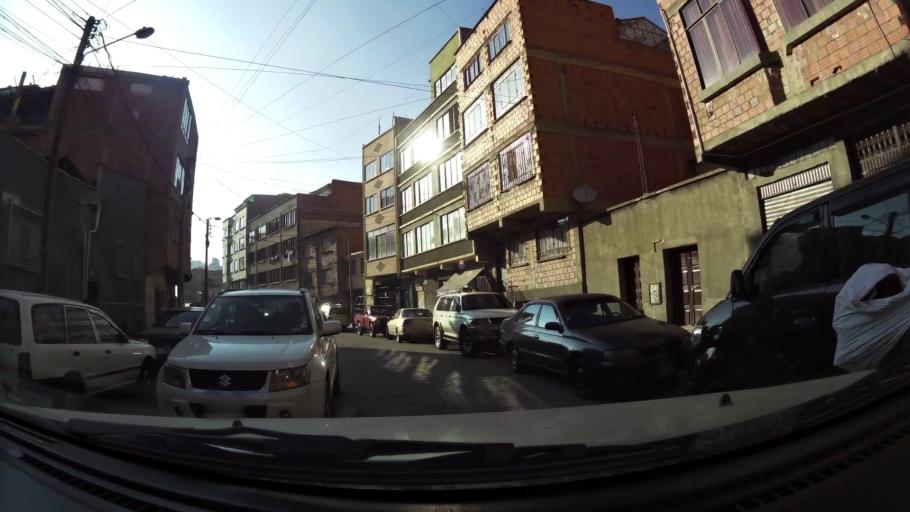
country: BO
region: La Paz
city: La Paz
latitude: -16.5013
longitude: -68.1380
